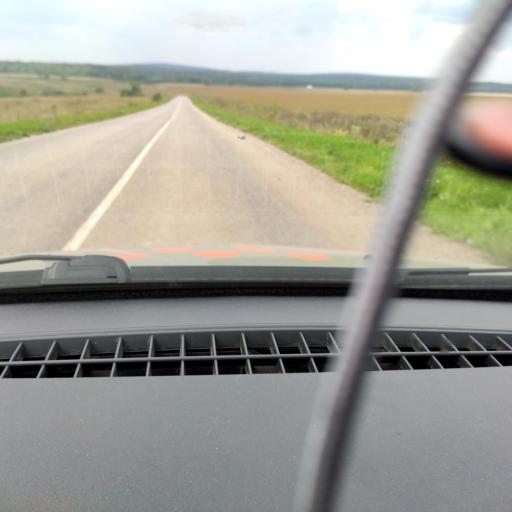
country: RU
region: Bashkortostan
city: Iglino
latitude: 54.7733
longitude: 56.5505
